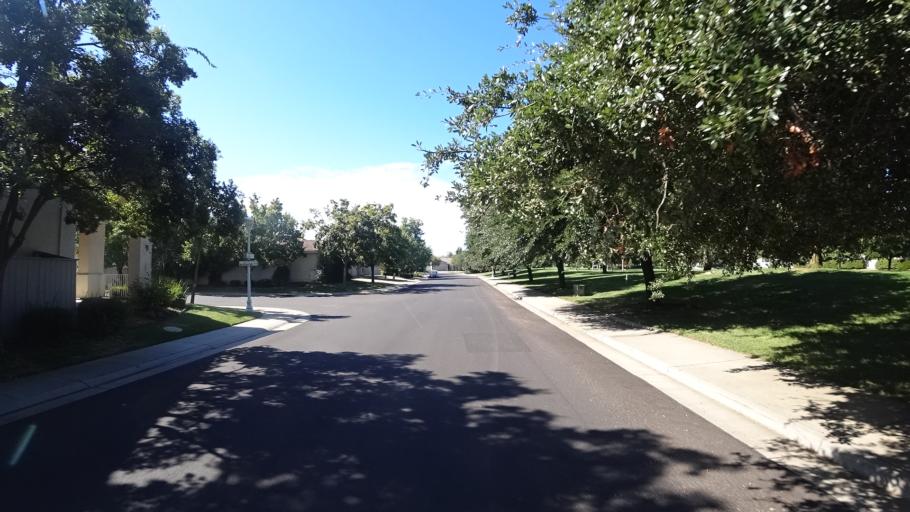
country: US
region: California
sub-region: Sacramento County
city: Laguna
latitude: 38.4184
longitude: -121.4783
